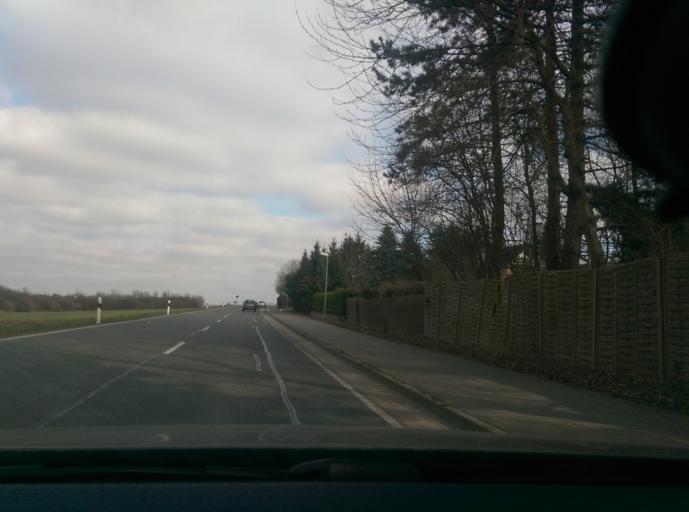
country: DE
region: Lower Saxony
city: Rehren
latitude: 52.2311
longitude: 9.2424
